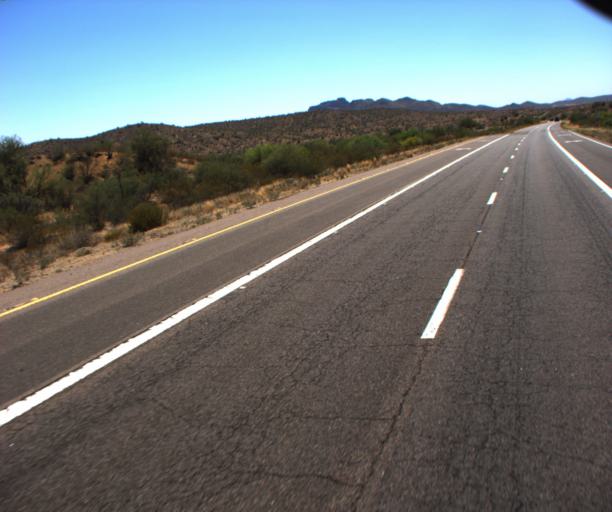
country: US
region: Arizona
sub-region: Maricopa County
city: Fountain Hills
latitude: 33.5837
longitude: -111.6144
